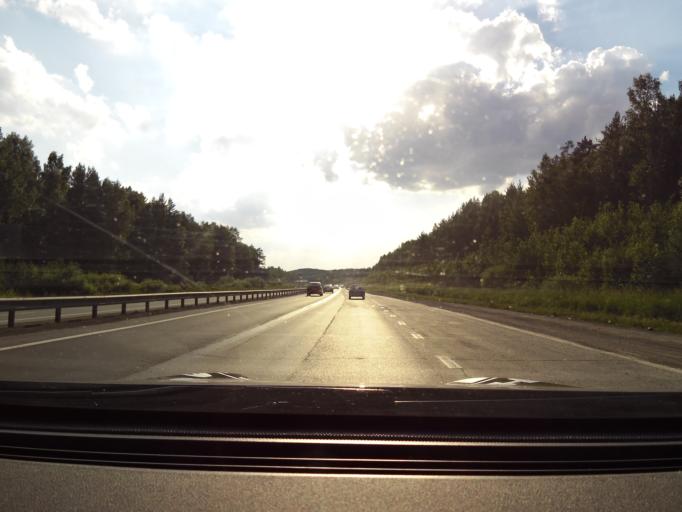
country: RU
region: Sverdlovsk
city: Severka
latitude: 56.8447
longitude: 60.2299
